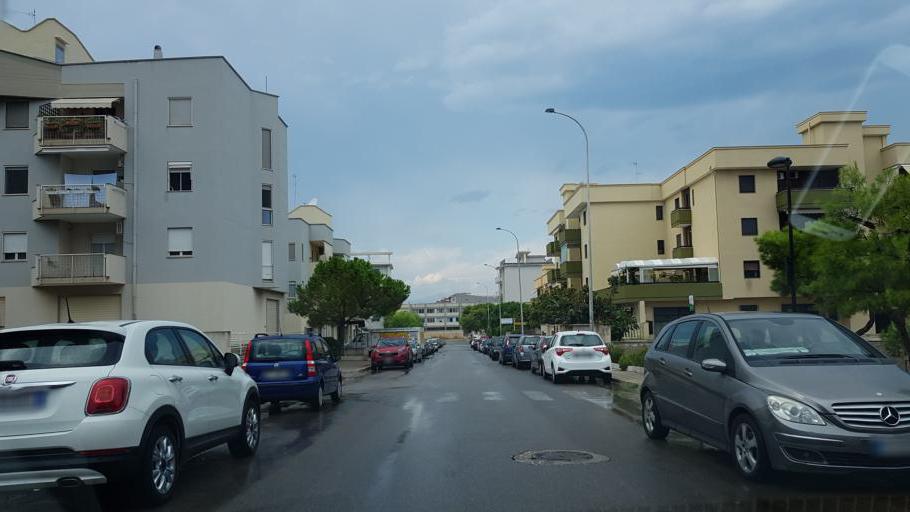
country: IT
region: Apulia
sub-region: Provincia di Bari
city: Monopoli
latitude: 40.9444
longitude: 17.3082
